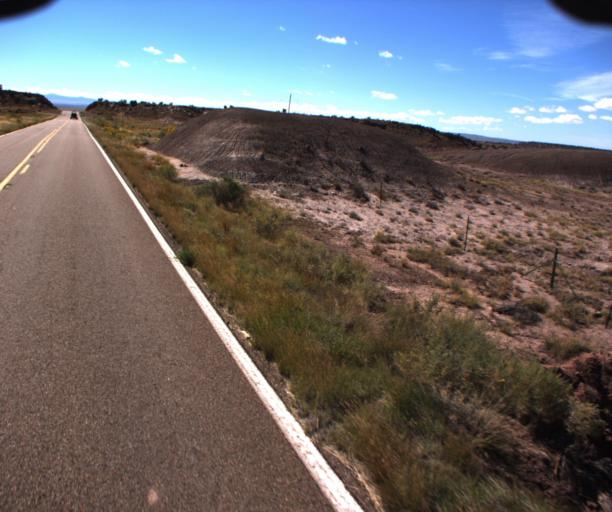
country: US
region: Arizona
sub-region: Apache County
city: Saint Johns
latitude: 34.6537
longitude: -109.2976
